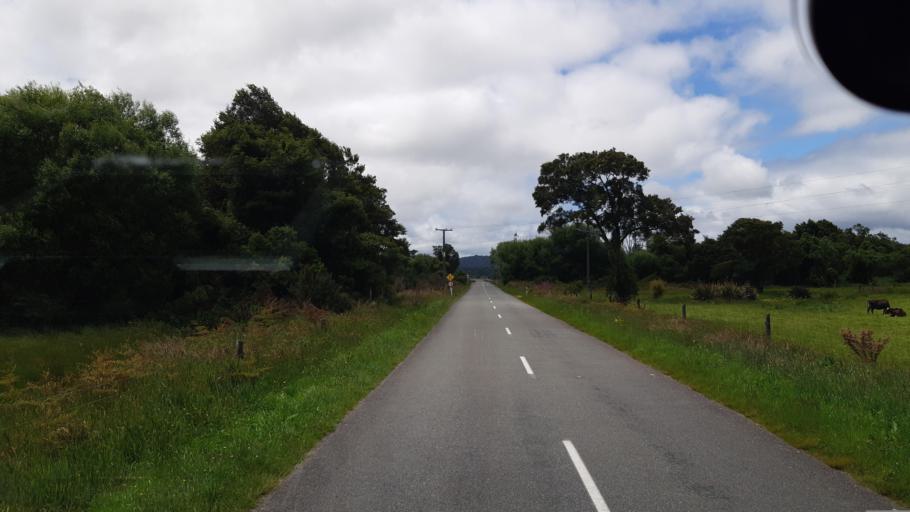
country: NZ
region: West Coast
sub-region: Grey District
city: Greymouth
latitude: -42.3165
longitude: 171.5356
